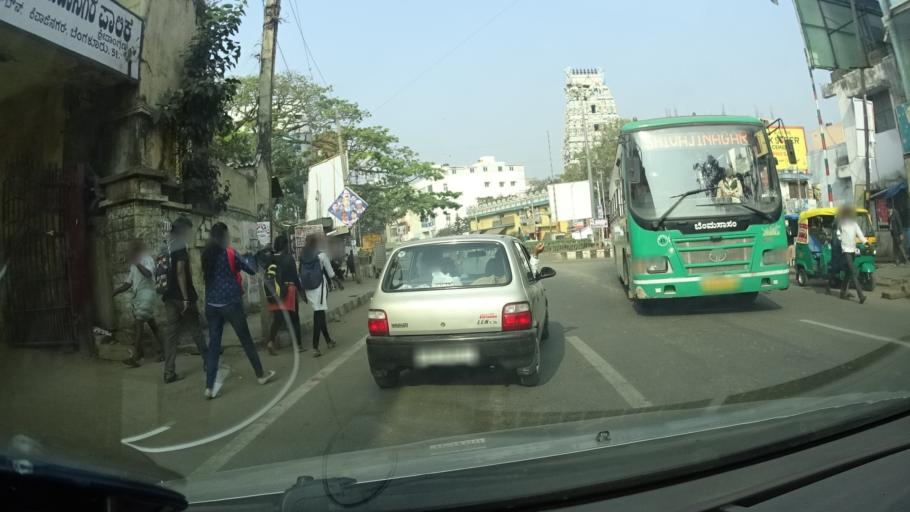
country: IN
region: Karnataka
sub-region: Bangalore Urban
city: Bangalore
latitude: 12.9844
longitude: 77.6021
